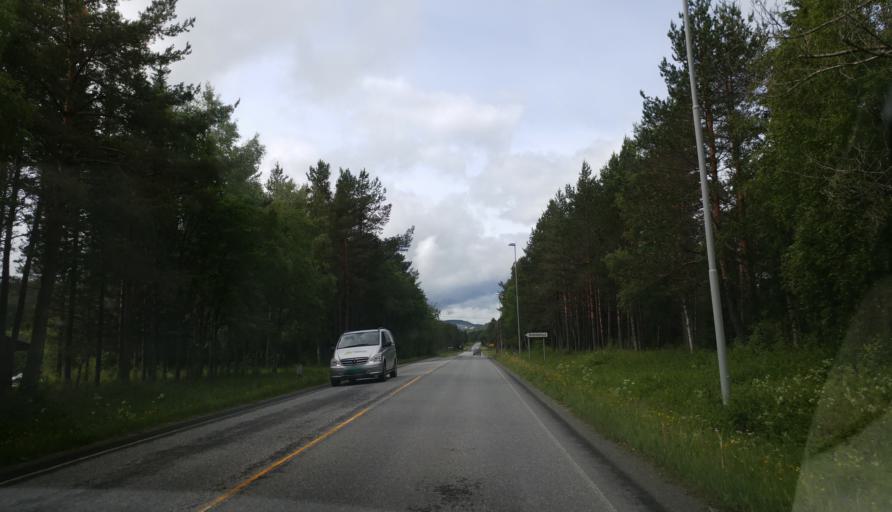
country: NO
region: Nord-Trondelag
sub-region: Stjordal
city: Stjordalshalsen
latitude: 63.3941
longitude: 11.0592
